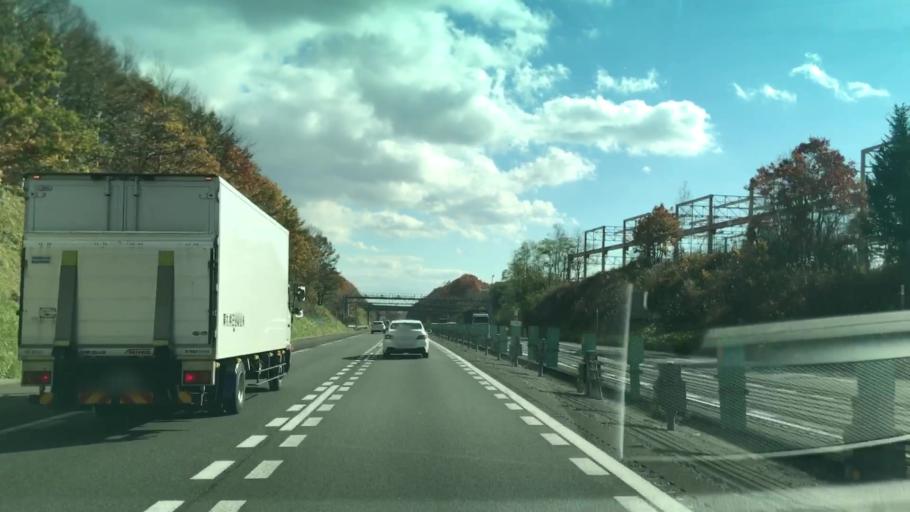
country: JP
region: Hokkaido
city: Kitahiroshima
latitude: 42.9345
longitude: 141.5275
